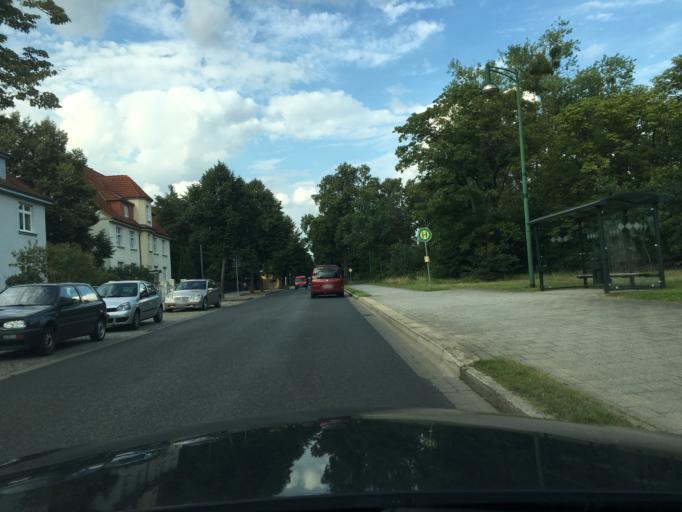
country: DE
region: Mecklenburg-Vorpommern
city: Neustrelitz
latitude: 53.3691
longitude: 13.0705
